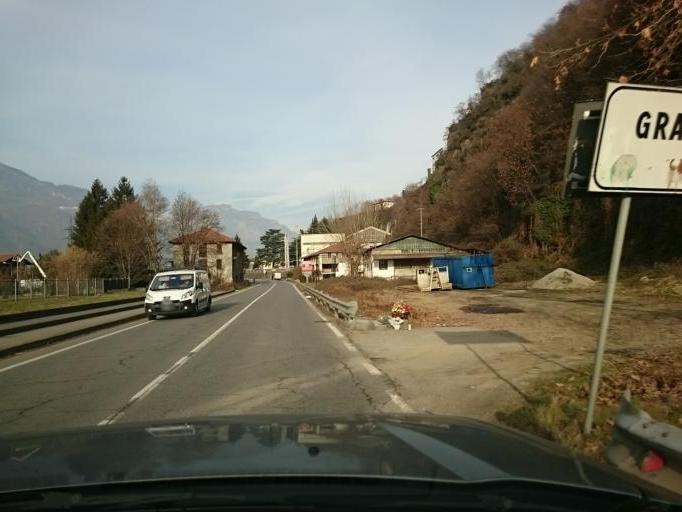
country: IT
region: Lombardy
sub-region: Provincia di Brescia
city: Gratacasolo
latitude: 45.8246
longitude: 10.1264
